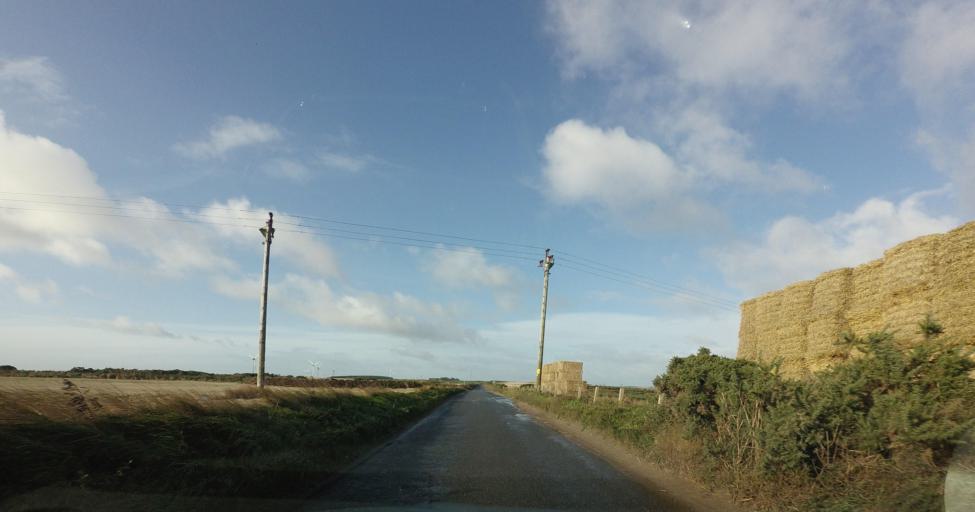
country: GB
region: Scotland
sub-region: Aberdeenshire
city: Whitehills
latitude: 57.6705
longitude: -2.5963
